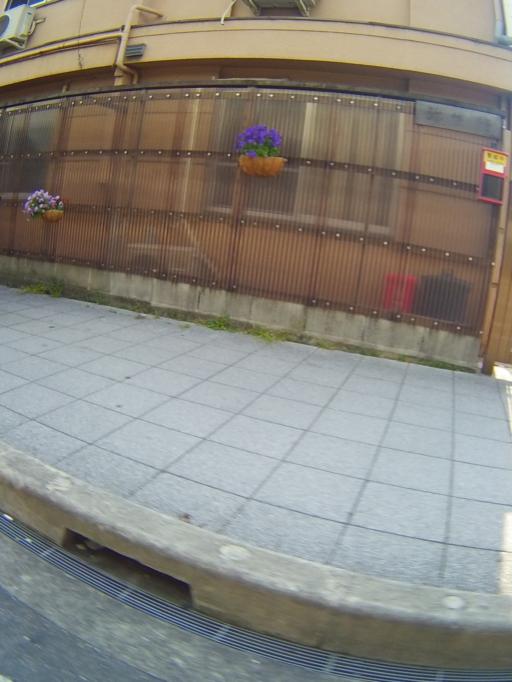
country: JP
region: Hyogo
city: Amagasaki
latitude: 34.6849
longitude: 135.4525
